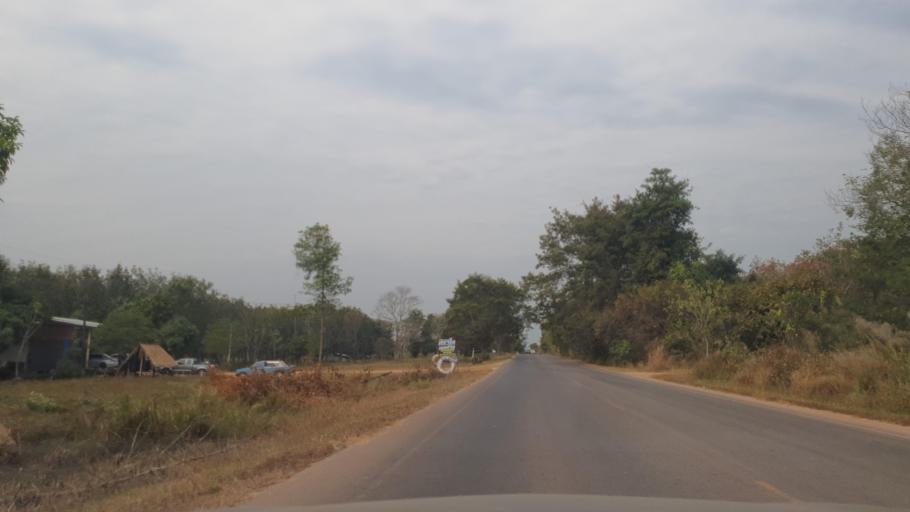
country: TH
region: Changwat Bueng Kan
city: Bung Khla
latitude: 18.2319
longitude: 104.0292
